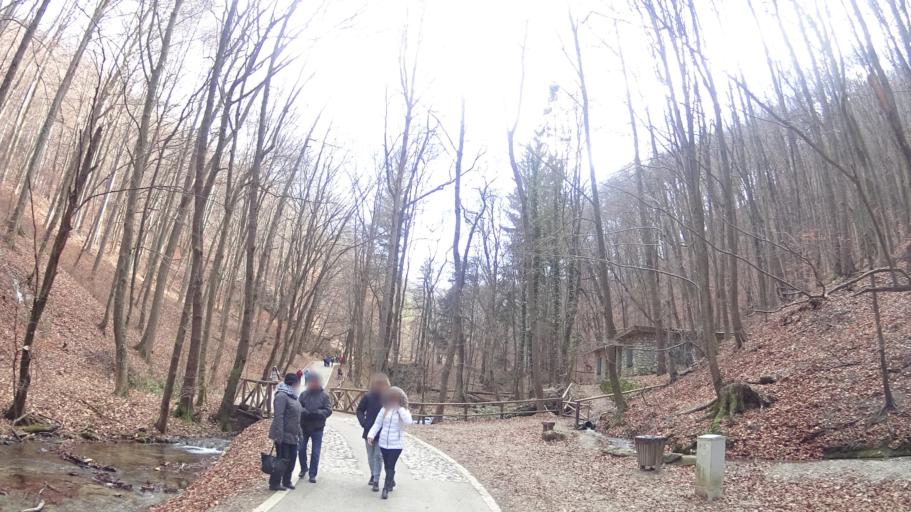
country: HU
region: Heves
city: Szilvasvarad
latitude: 48.0795
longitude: 20.4063
